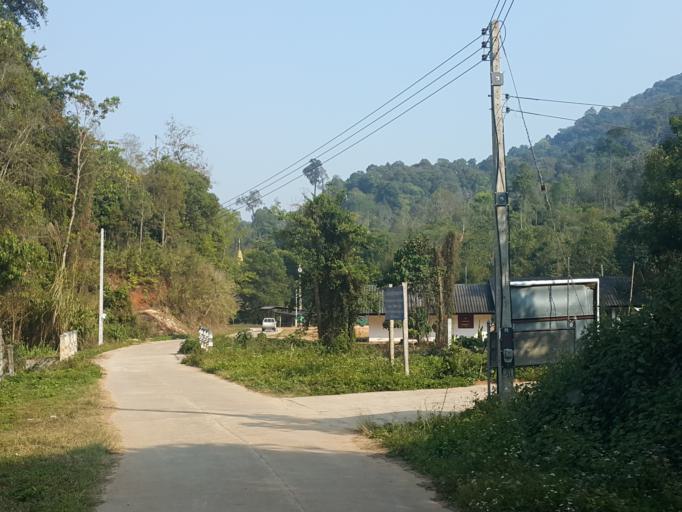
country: TH
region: Chiang Mai
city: Samoeng
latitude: 19.0179
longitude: 98.7585
